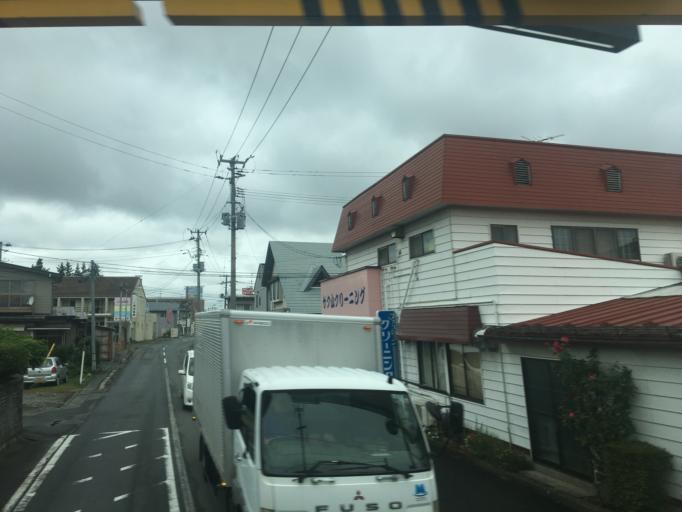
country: JP
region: Iwate
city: Morioka-shi
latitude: 39.7115
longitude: 141.1101
